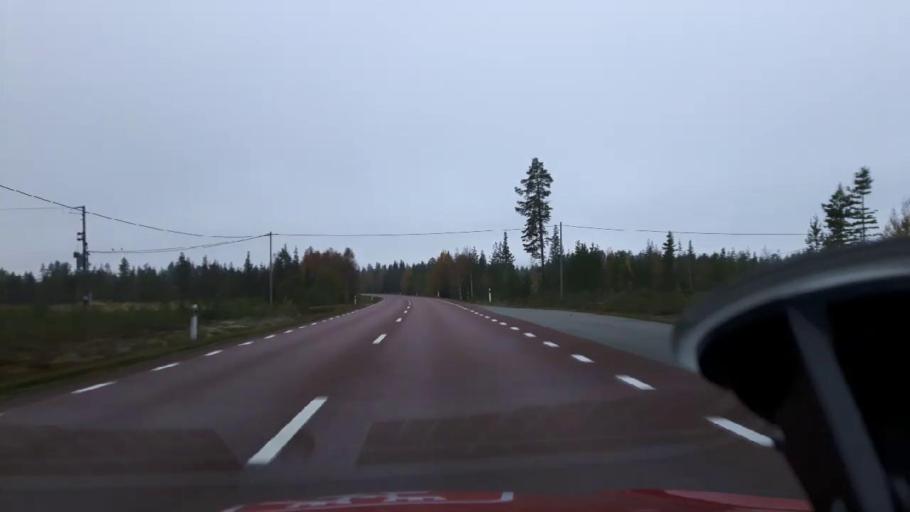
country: SE
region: Jaemtland
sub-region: Bergs Kommun
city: Hoverberg
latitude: 62.5113
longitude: 14.4497
